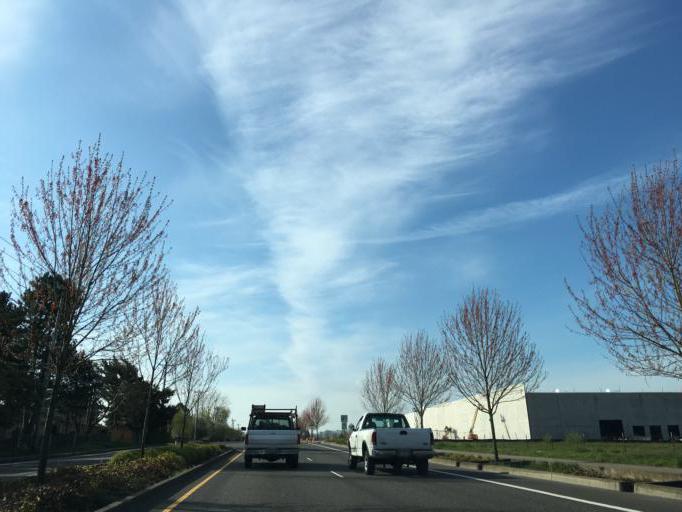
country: US
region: Oregon
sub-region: Multnomah County
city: Wood Village
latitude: 45.5266
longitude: -122.4132
